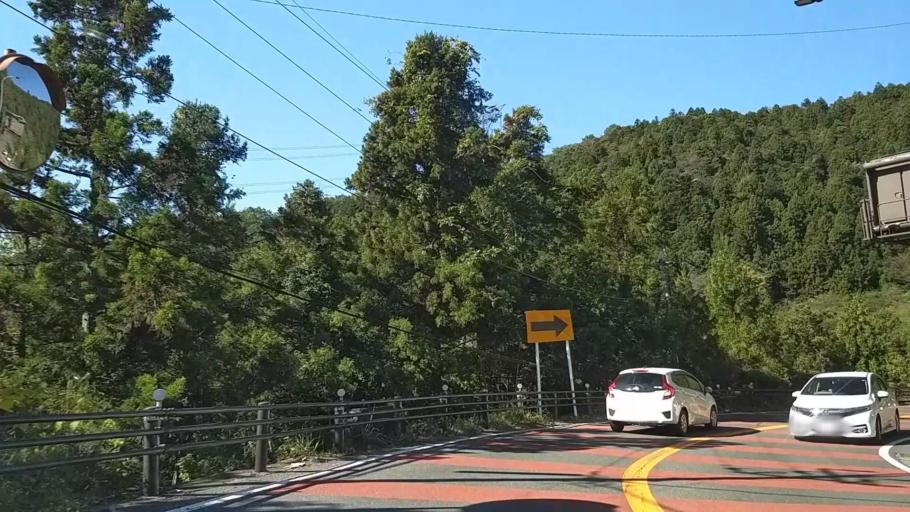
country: JP
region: Yamanashi
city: Uenohara
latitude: 35.6178
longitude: 139.2213
